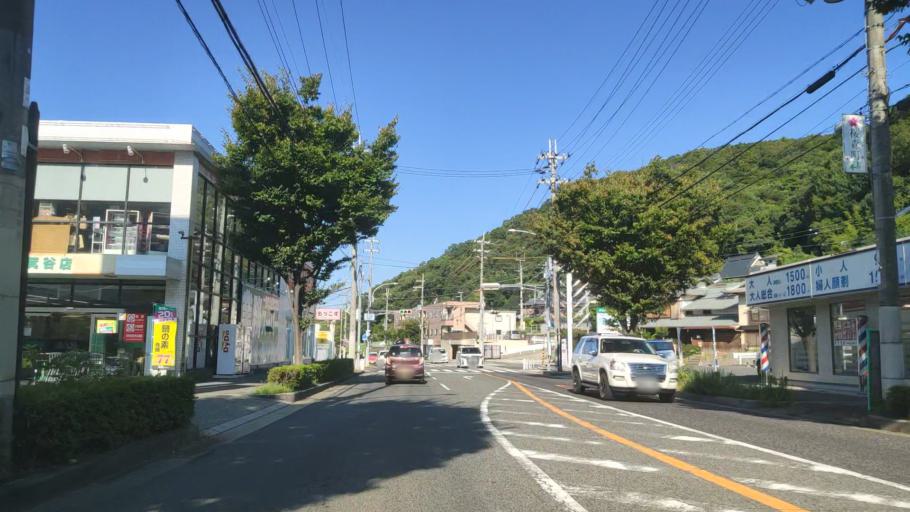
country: JP
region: Hyogo
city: Kobe
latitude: 34.7612
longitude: 135.1637
